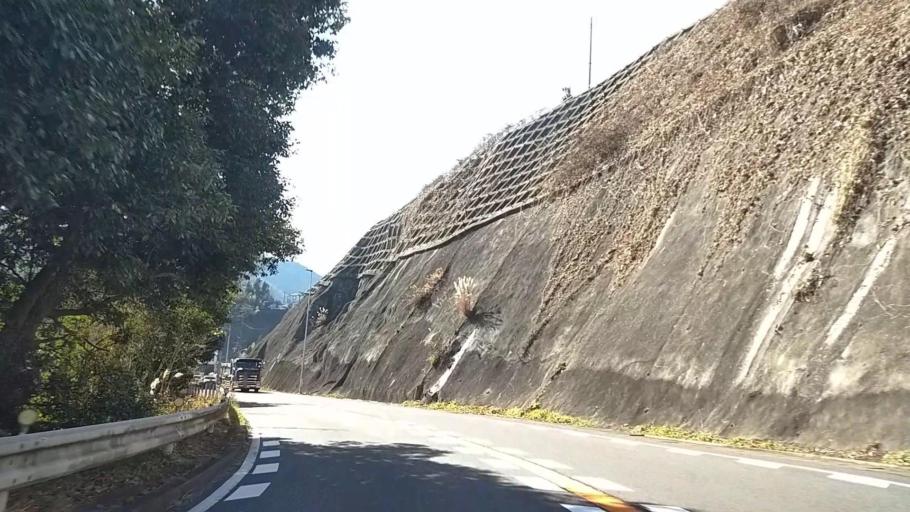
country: JP
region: Yamanashi
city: Uenohara
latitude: 35.6189
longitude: 139.1712
